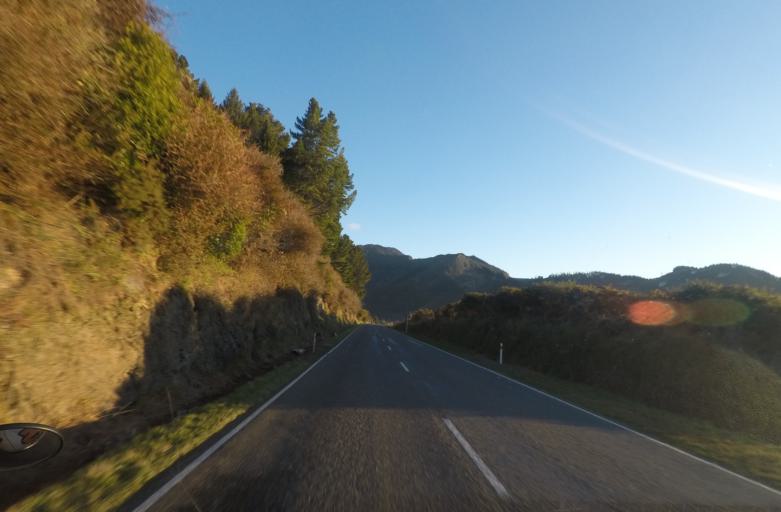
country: NZ
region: Marlborough
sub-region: Marlborough District
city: Picton
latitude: -41.2897
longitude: 173.6775
